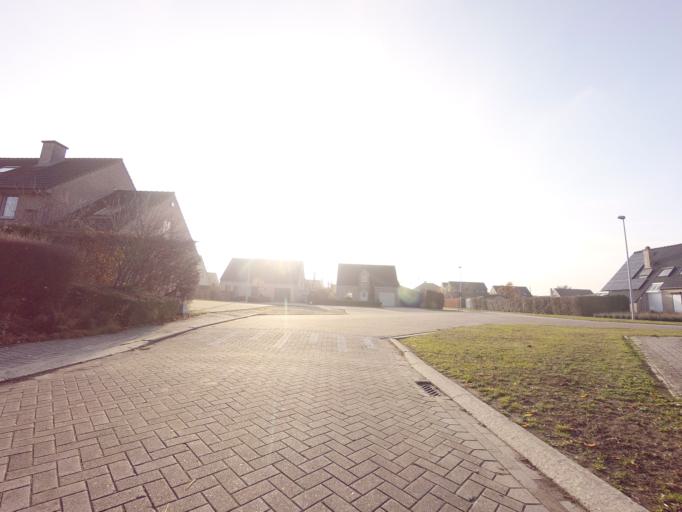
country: BE
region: Flanders
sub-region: Provincie Vlaams-Brabant
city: Herent
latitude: 50.9412
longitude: 4.6515
